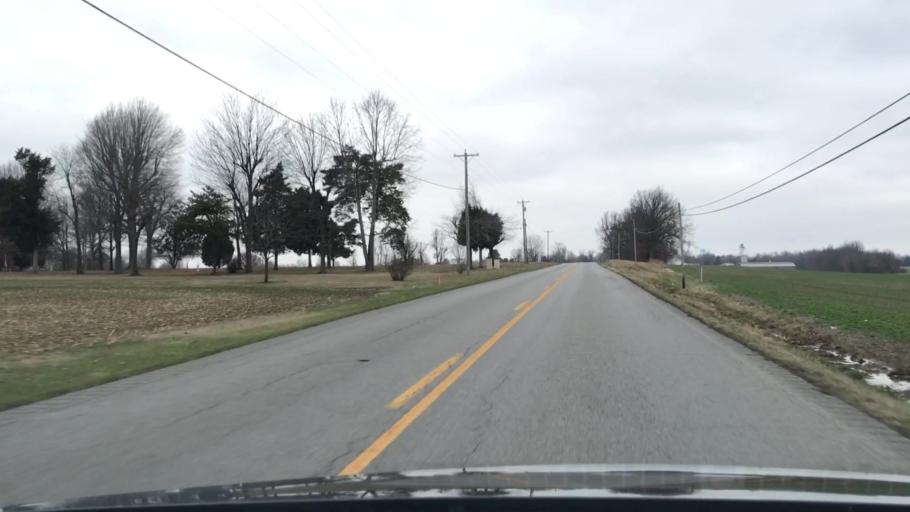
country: US
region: Kentucky
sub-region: Muhlenberg County
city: Morehead
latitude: 37.3927
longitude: -87.2556
